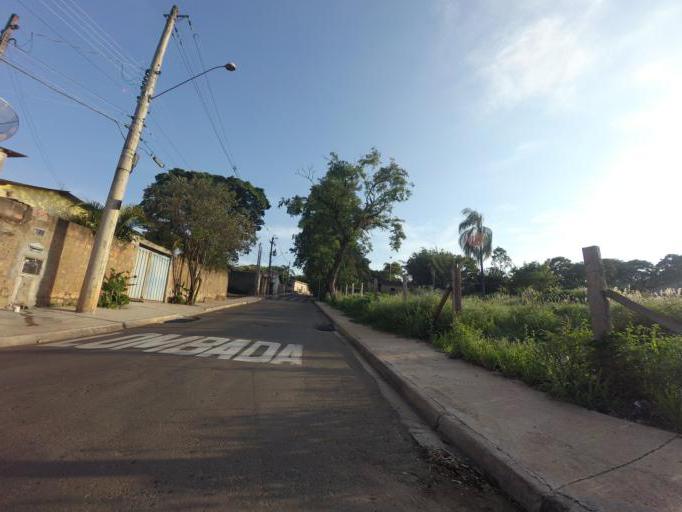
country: BR
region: Sao Paulo
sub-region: Piracicaba
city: Piracicaba
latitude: -22.7493
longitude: -47.6101
